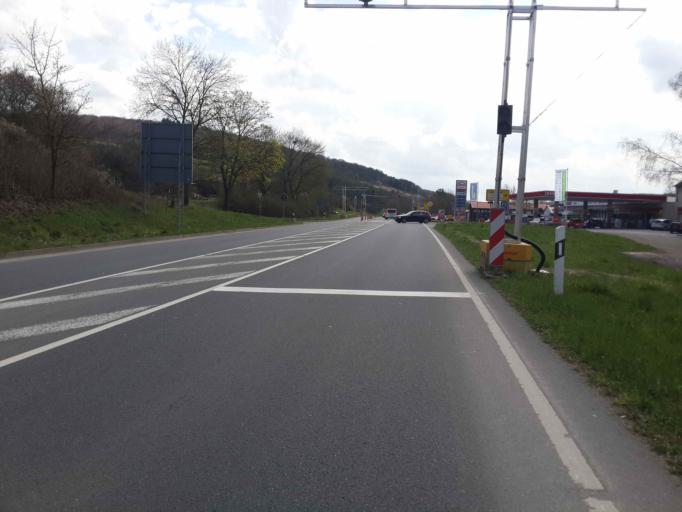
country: DE
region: Baden-Wuerttemberg
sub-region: Regierungsbezirk Stuttgart
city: Bad Mergentheim
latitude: 49.4774
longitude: 9.7712
